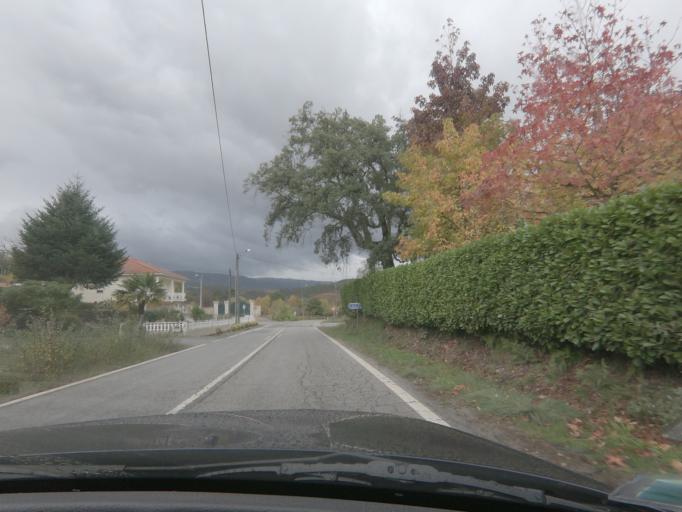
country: PT
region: Vila Real
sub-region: Mondim de Basto
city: Mondim de Basto
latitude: 41.3964
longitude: -7.9599
